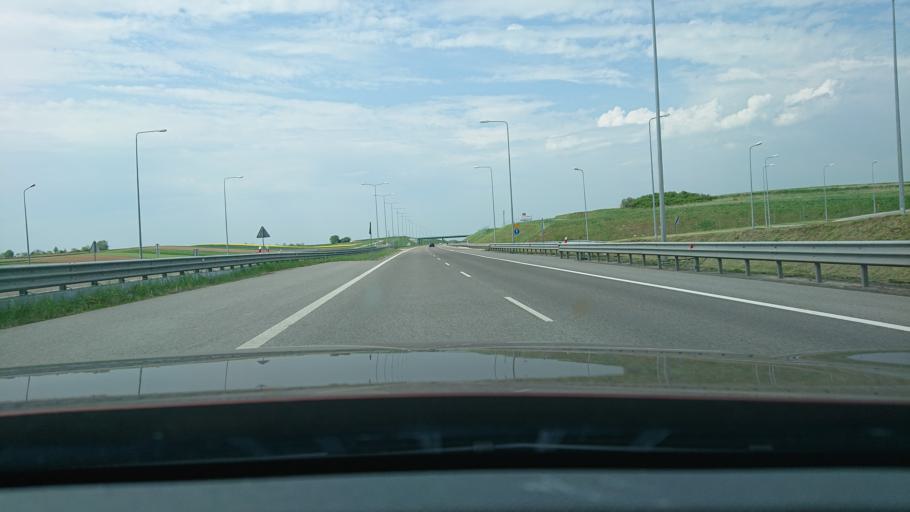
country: PL
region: Subcarpathian Voivodeship
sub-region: Powiat jaroslawski
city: Wierzbna
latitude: 50.0063
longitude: 22.5984
